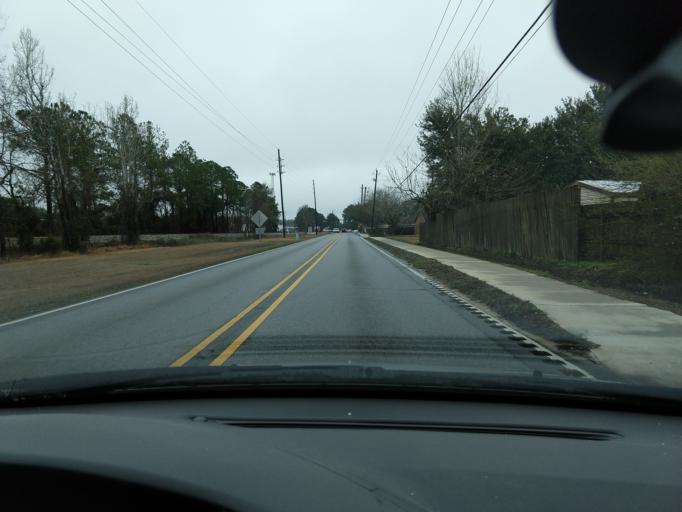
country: US
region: Mississippi
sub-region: Jackson County
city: Gulf Park Estates
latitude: 30.4108
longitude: -88.7886
